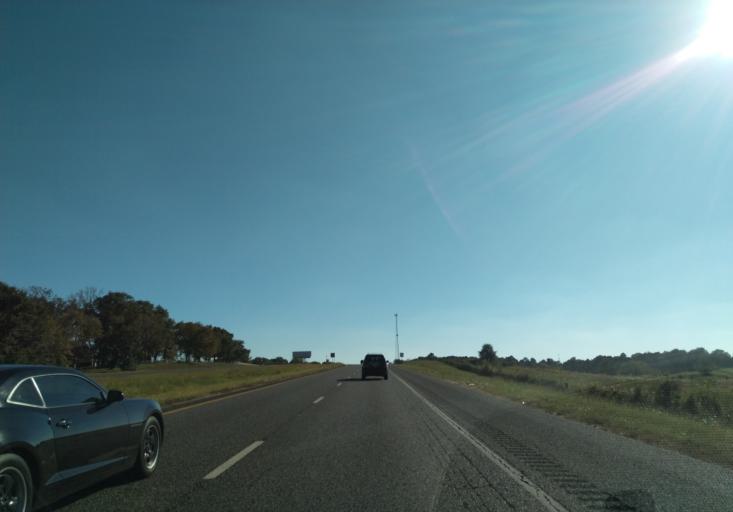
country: US
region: Texas
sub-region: Waller County
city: Hempstead
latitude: 30.1786
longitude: -96.0648
